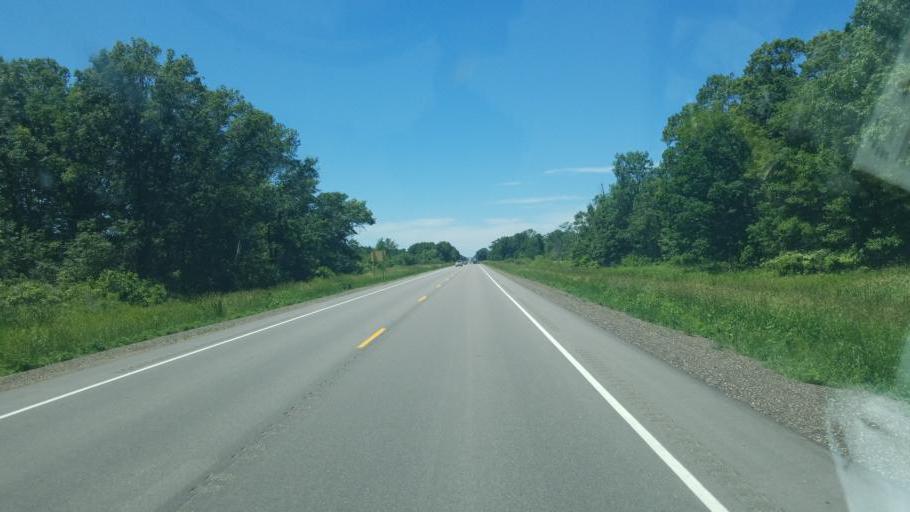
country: US
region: Wisconsin
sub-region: Juneau County
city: New Lisbon
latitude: 44.0258
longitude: -90.2561
